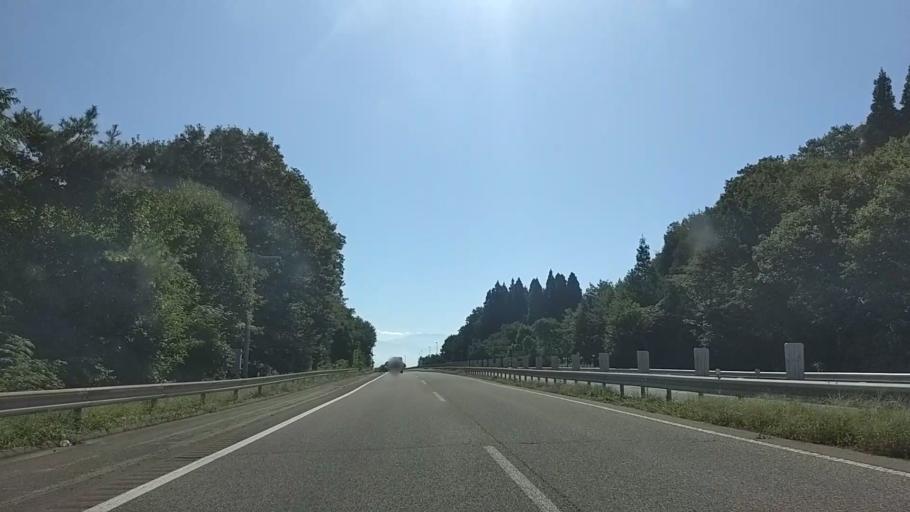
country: JP
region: Toyama
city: Kuragaki-kosugi
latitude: 36.6849
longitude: 137.1027
